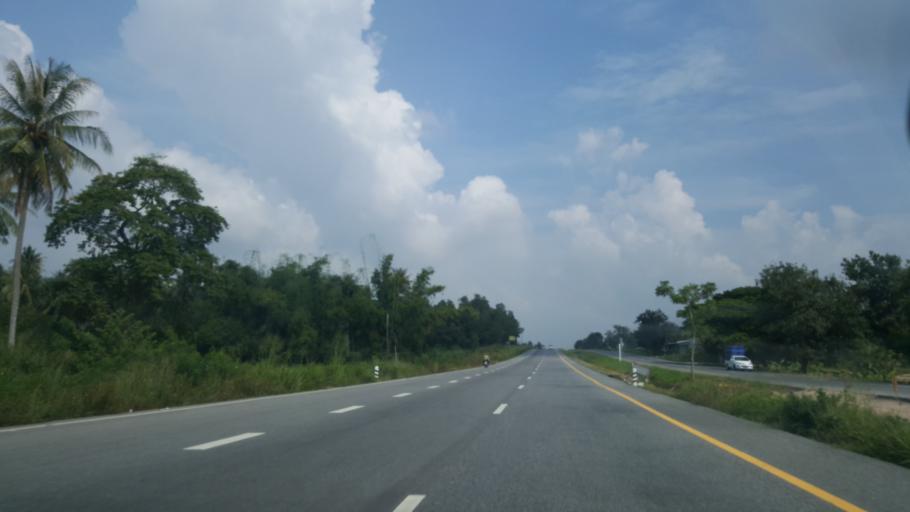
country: TH
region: Rayong
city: Ban Chang
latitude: 12.7934
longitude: 100.9919
